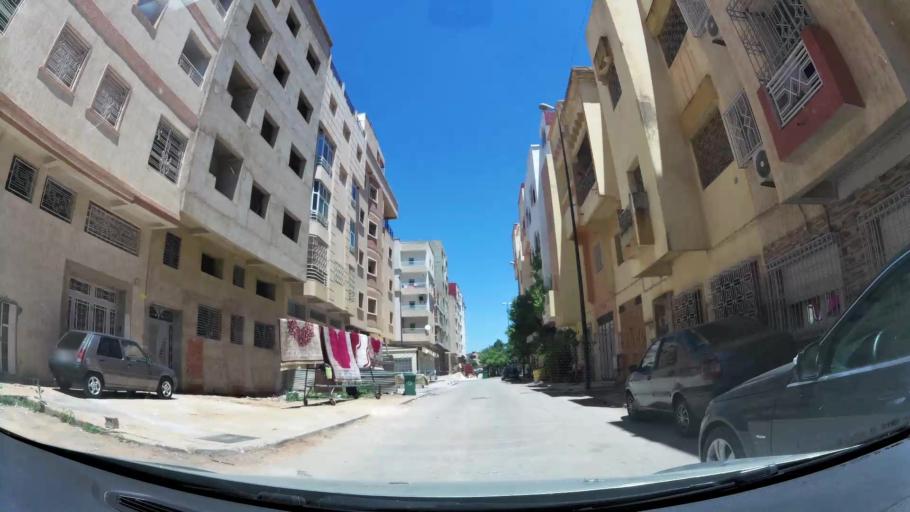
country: MA
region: Meknes-Tafilalet
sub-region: Meknes
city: Meknes
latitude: 33.8618
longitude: -5.5767
